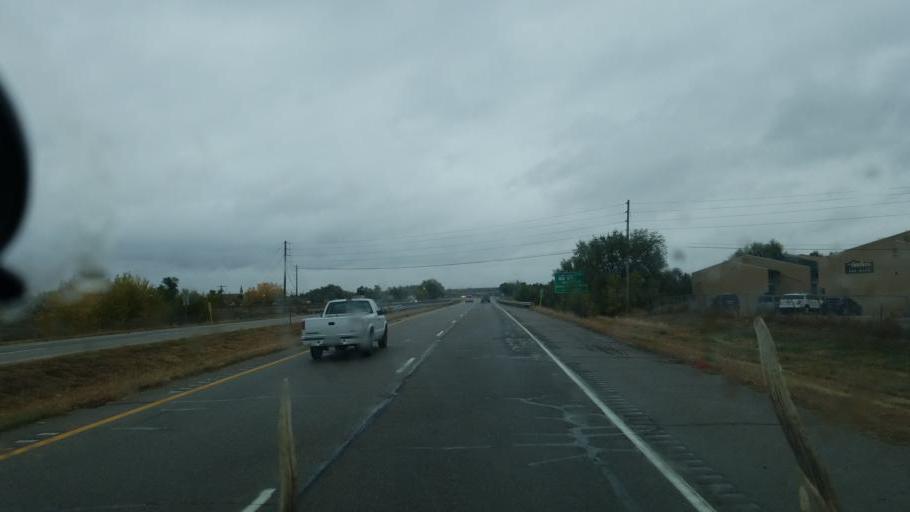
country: US
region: Colorado
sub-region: Pueblo County
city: Pueblo
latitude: 38.2811
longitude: -104.5697
